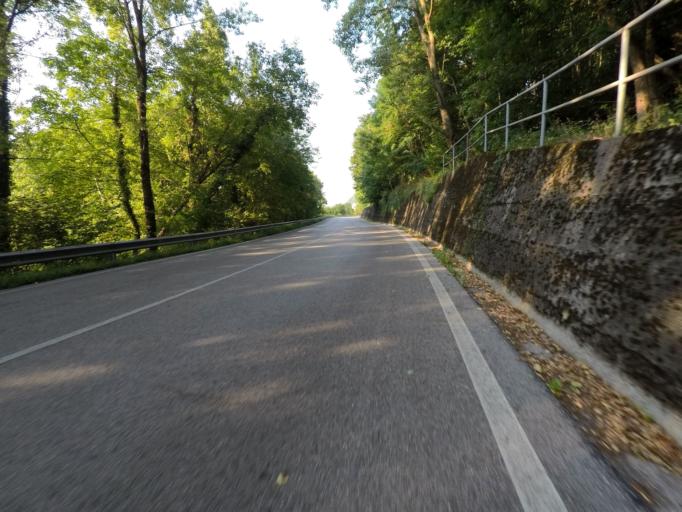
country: IT
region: Friuli Venezia Giulia
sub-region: Provincia di Udine
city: Trasaghis
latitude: 46.2642
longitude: 13.0436
